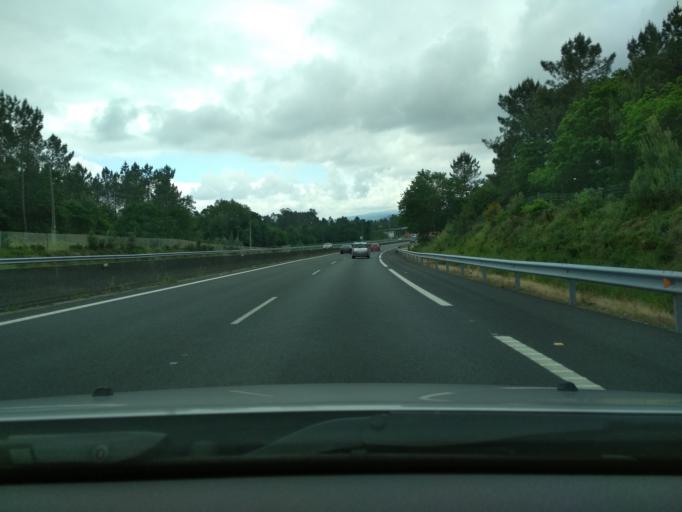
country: ES
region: Galicia
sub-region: Provincia da Coruna
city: Santiago de Compostela
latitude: 42.8224
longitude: -8.5706
